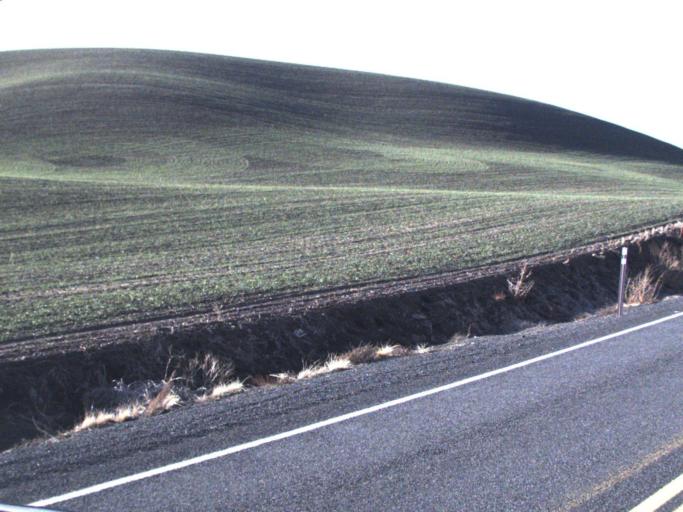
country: US
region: Washington
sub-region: Whitman County
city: Colfax
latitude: 46.7624
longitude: -117.4312
